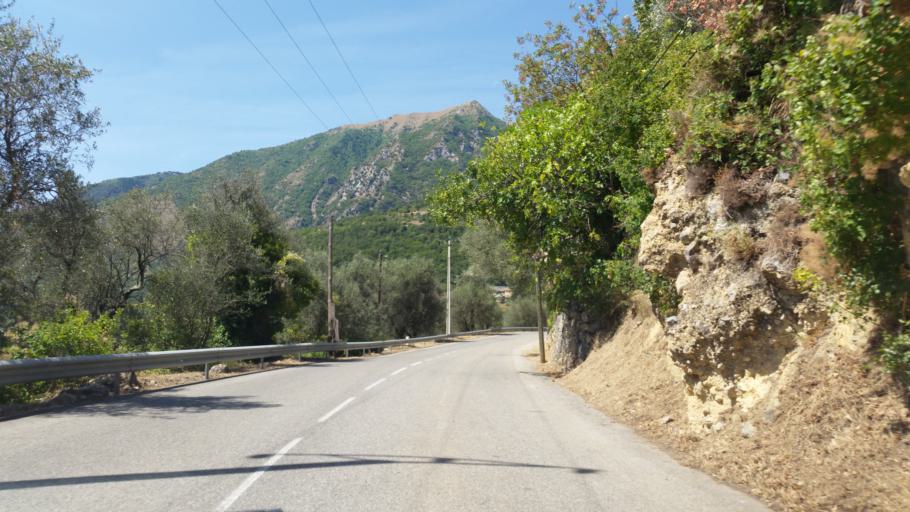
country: FR
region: Provence-Alpes-Cote d'Azur
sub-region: Departement des Alpes-Maritimes
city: Breil-sur-Roya
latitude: 43.9427
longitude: 7.5022
